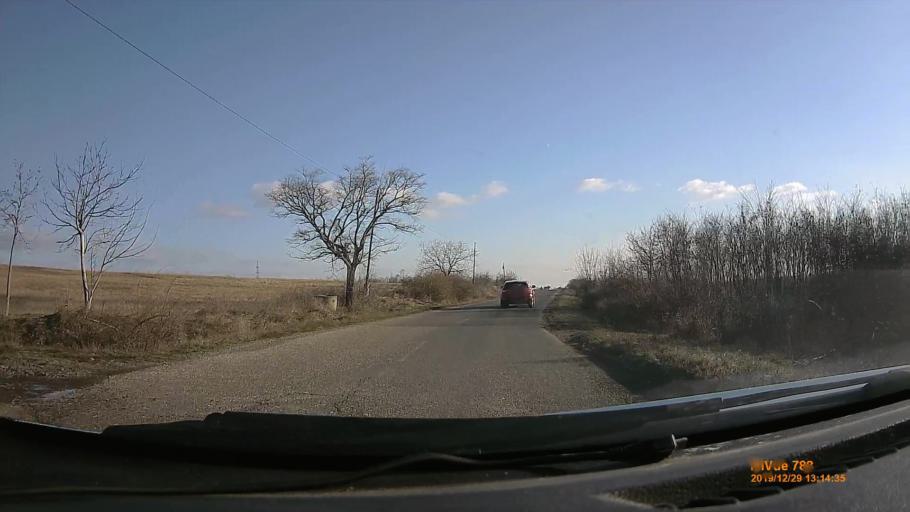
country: HU
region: Heves
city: Domoszlo
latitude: 47.8311
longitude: 20.0993
